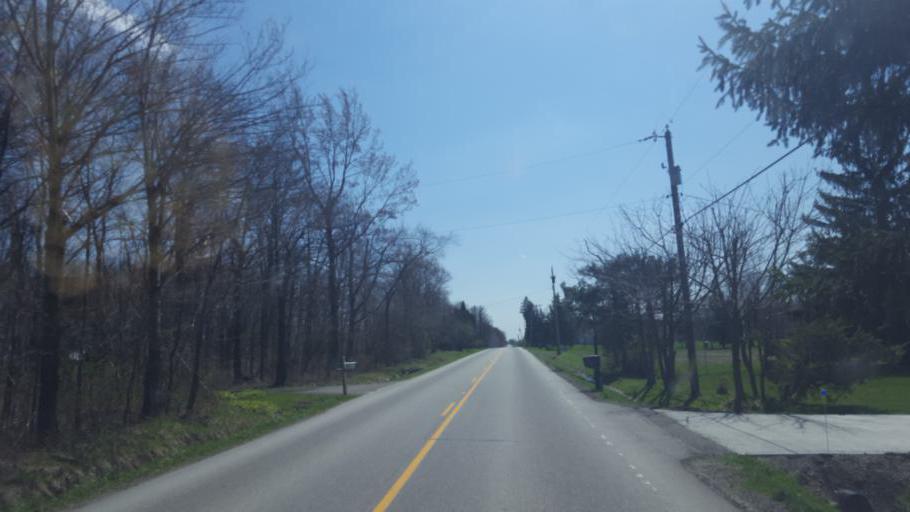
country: US
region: Ohio
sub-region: Geauga County
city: Middlefield
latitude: 41.3971
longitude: -81.1084
